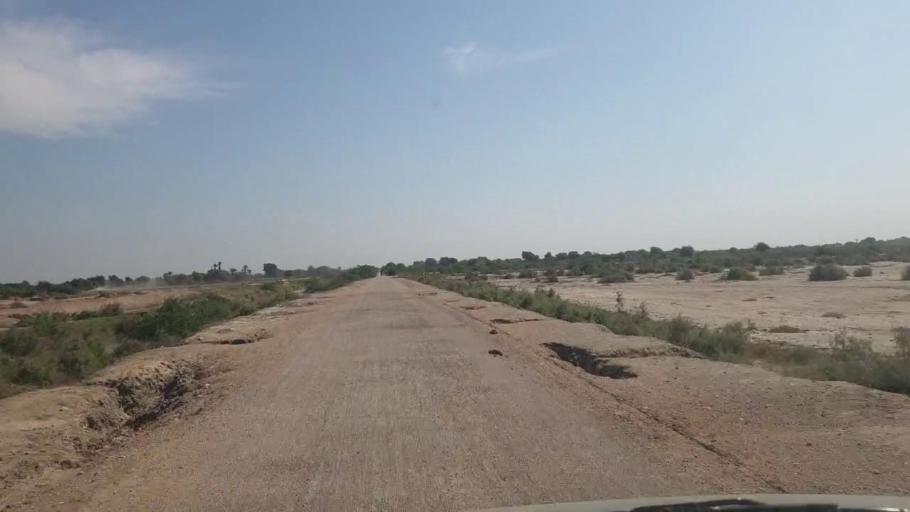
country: PK
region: Sindh
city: Digri
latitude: 24.9605
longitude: 69.1289
